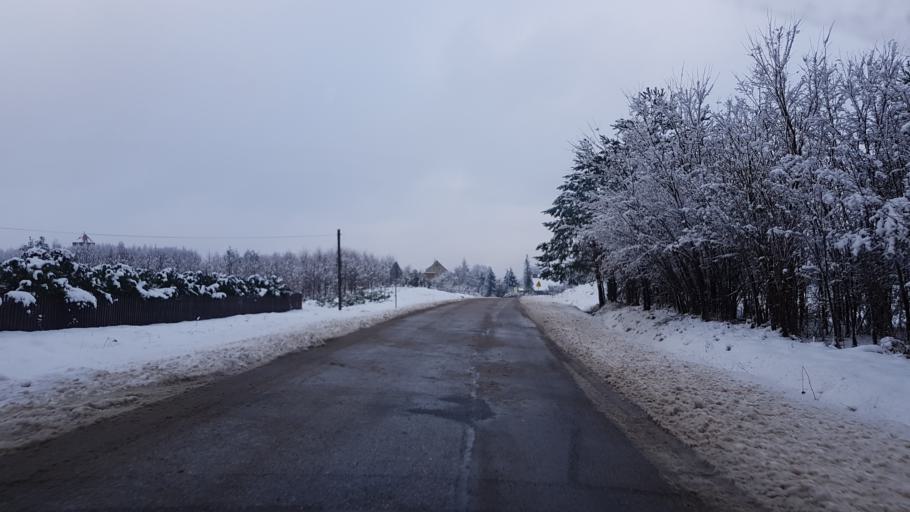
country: PL
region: West Pomeranian Voivodeship
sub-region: Powiat drawski
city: Zlocieniec
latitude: 53.5198
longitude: 16.0055
